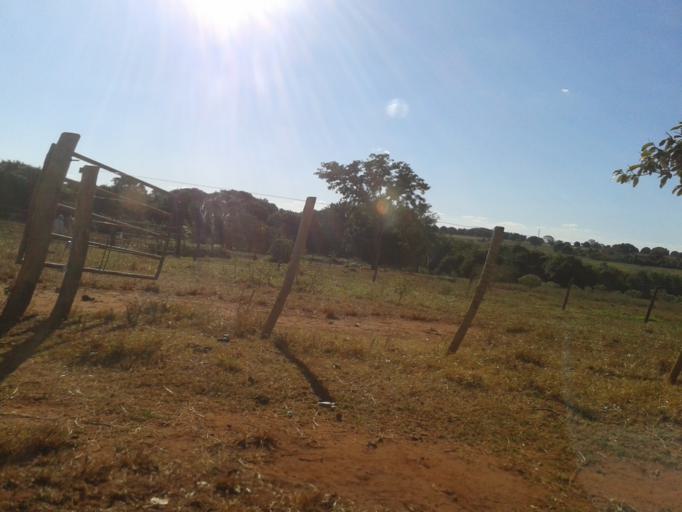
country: BR
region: Minas Gerais
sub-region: Centralina
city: Centralina
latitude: -18.7373
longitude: -49.1815
